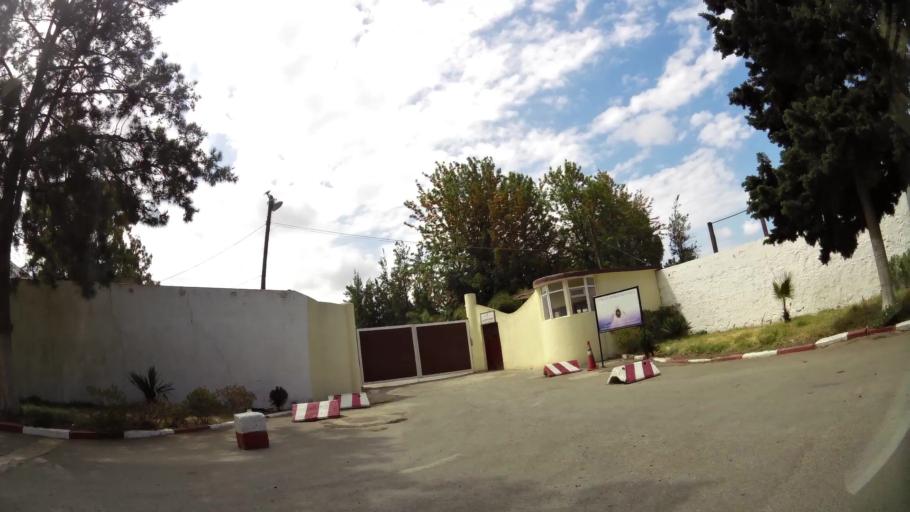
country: MA
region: Gharb-Chrarda-Beni Hssen
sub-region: Kenitra Province
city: Kenitra
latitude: 34.2519
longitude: -6.5929
